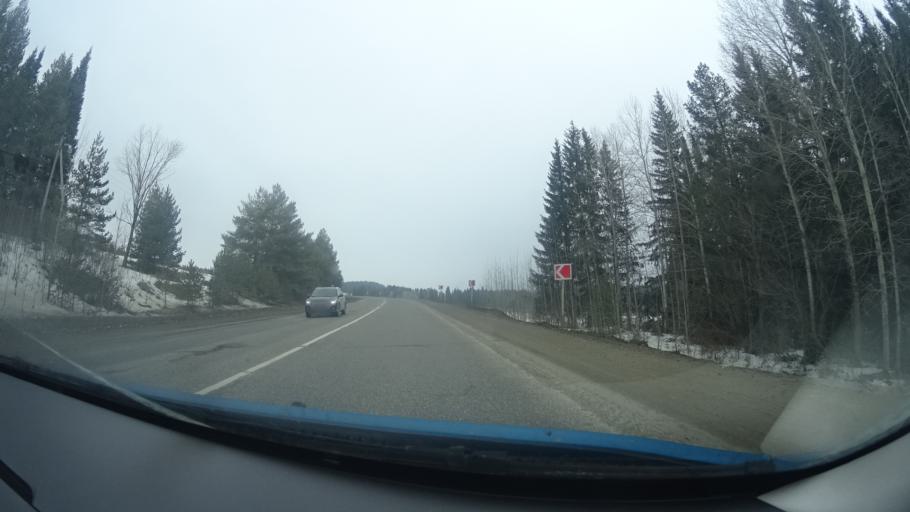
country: RU
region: Perm
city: Osa
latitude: 57.3058
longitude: 55.6197
